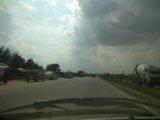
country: IN
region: Karnataka
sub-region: Bangalore Rural
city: Dasarahalli
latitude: 13.1308
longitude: 77.9570
